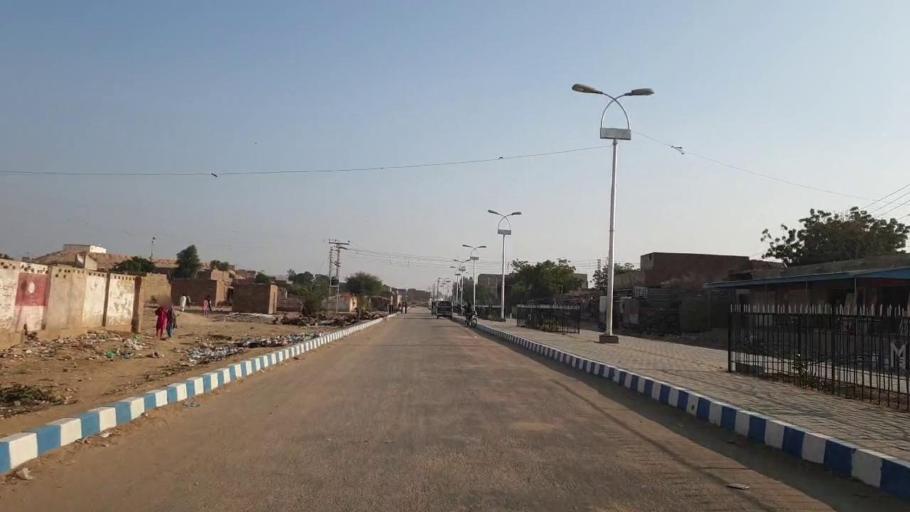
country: PK
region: Sindh
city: Kotri
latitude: 25.3615
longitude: 68.2602
